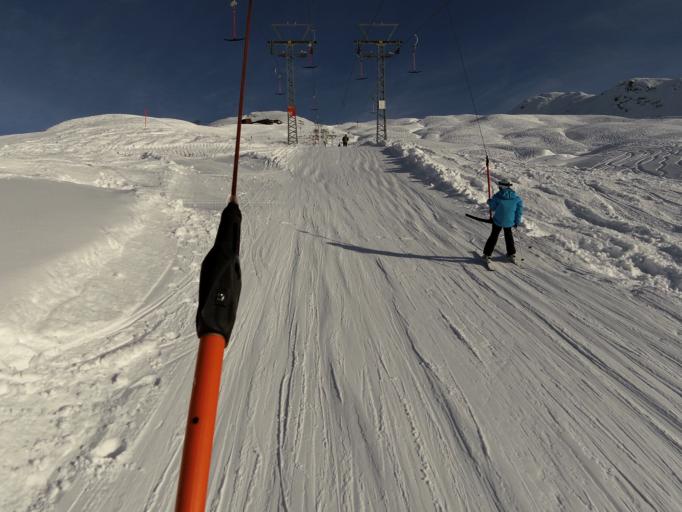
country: CH
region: Grisons
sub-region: Praettigau/Davos District
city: Davos
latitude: 46.8022
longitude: 9.9130
